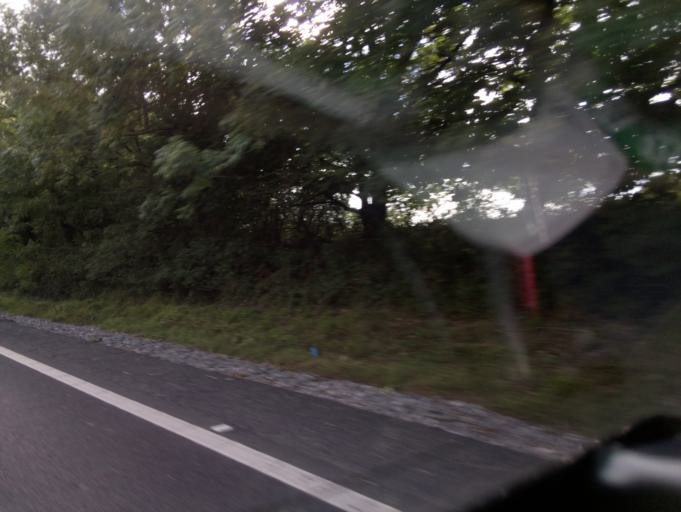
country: GB
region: England
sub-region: Devon
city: Bovey Tracey
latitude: 50.5475
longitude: -3.6894
